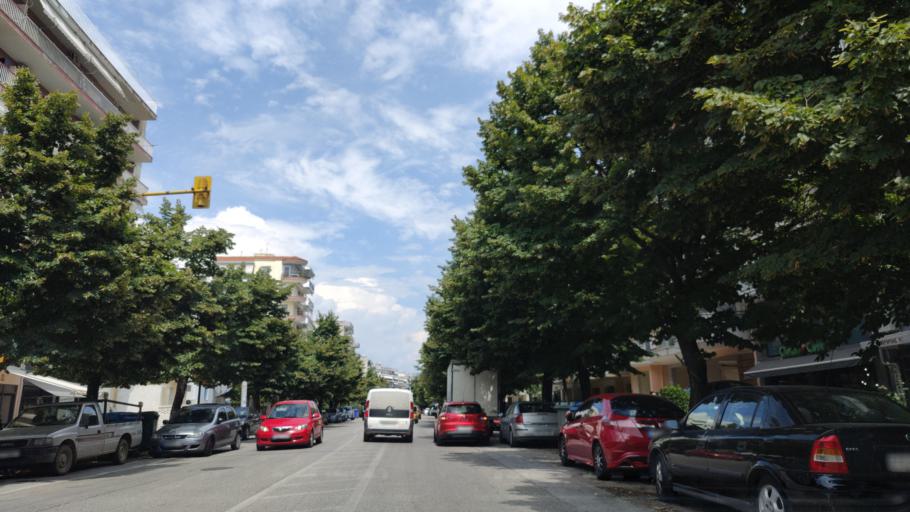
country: GR
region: Central Macedonia
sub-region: Nomos Serron
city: Serres
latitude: 41.0827
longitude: 23.5430
